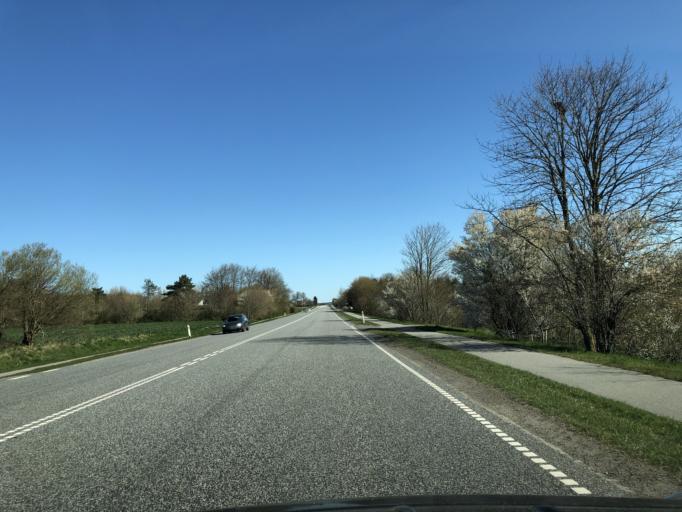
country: DK
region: North Denmark
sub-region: Rebild Kommune
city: Stovring
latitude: 56.9108
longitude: 9.8497
